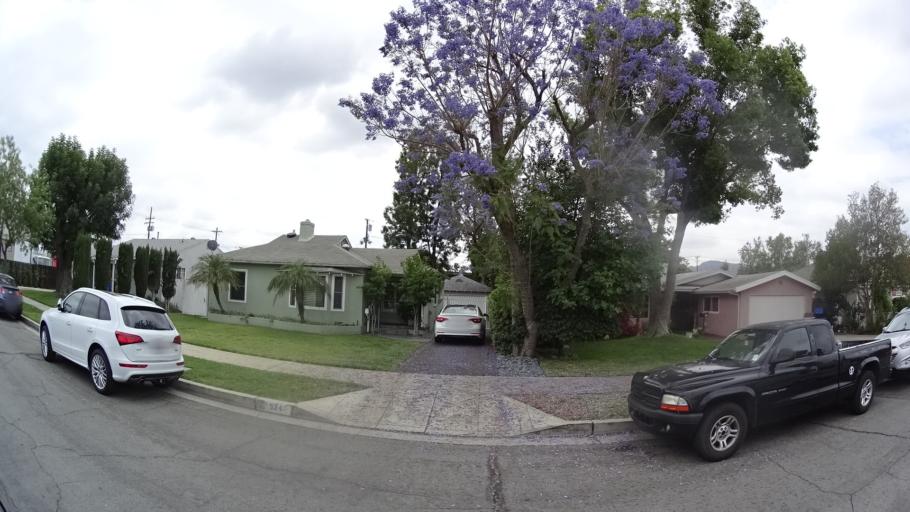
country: US
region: California
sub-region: Los Angeles County
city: Burbank
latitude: 34.1745
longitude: -118.3182
